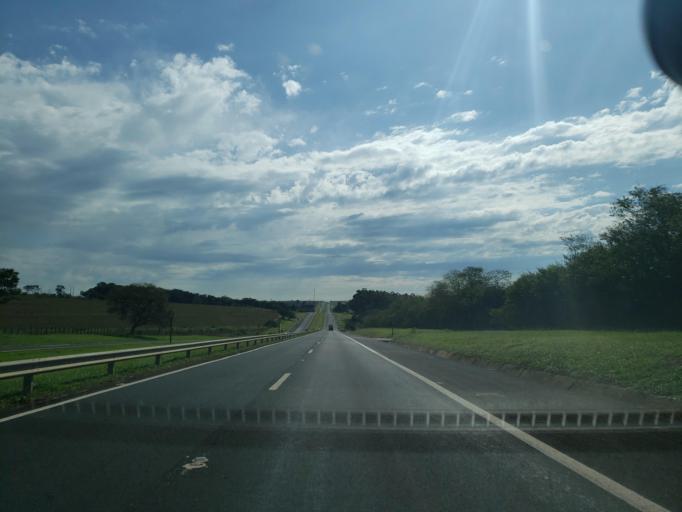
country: BR
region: Sao Paulo
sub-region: Cafelandia
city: Cafelandia
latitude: -21.8971
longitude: -49.5337
